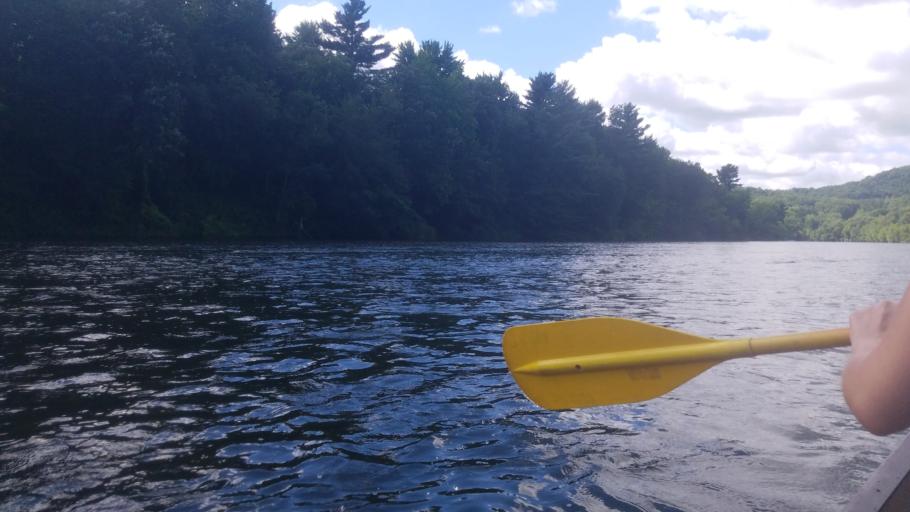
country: US
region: Wisconsin
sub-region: Dunn County
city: Menomonie
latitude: 44.8425
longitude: -91.9508
